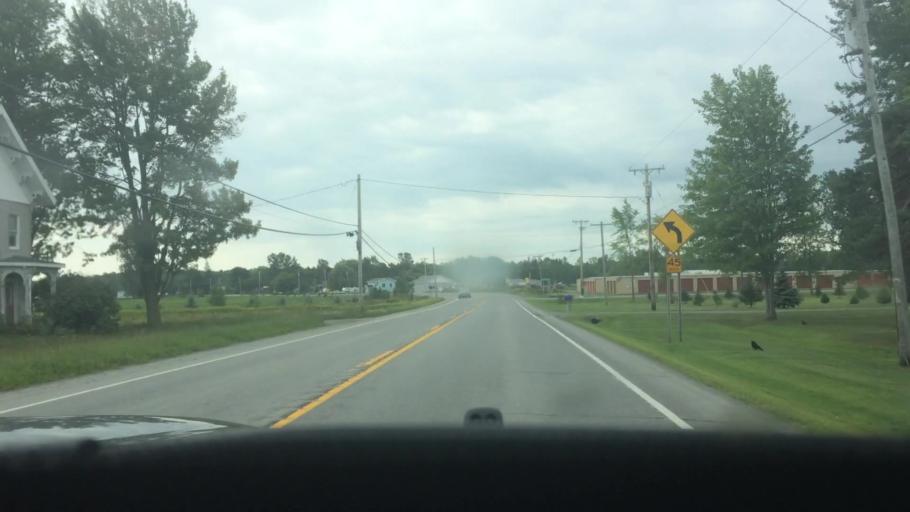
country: US
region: New York
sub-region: St. Lawrence County
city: Ogdensburg
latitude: 44.6653
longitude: -75.4673
